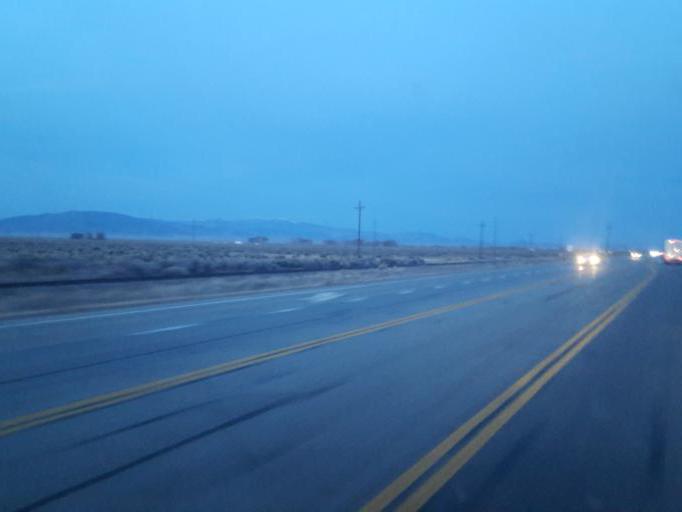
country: US
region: Colorado
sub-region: Alamosa County
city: Alamosa
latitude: 37.5115
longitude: -105.9802
